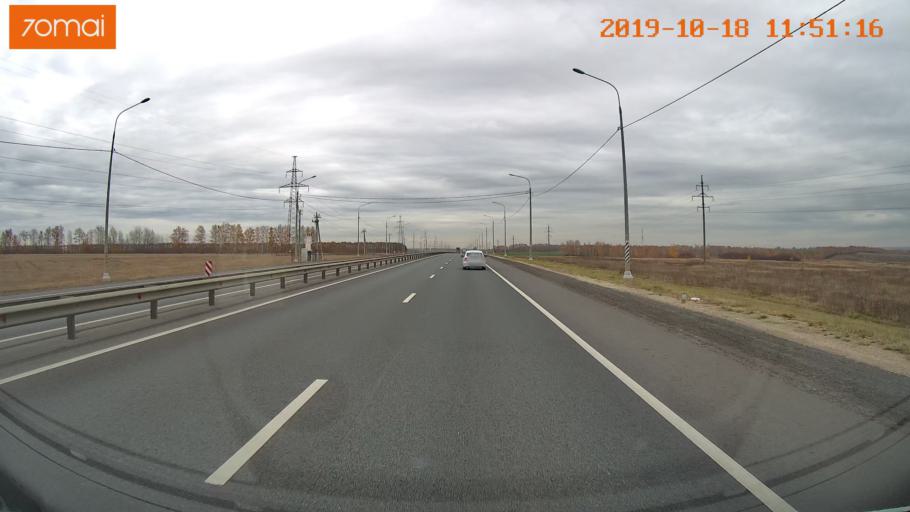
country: RU
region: Rjazan
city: Mikhaylov
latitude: 54.2568
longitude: 39.0215
